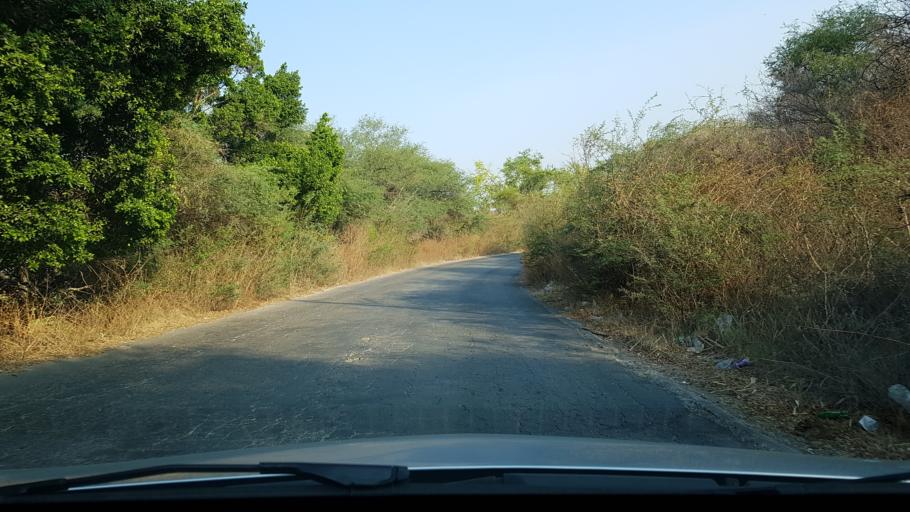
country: MX
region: Morelos
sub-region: Tepalcingo
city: Zacapalco
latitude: 18.6370
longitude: -99.0166
